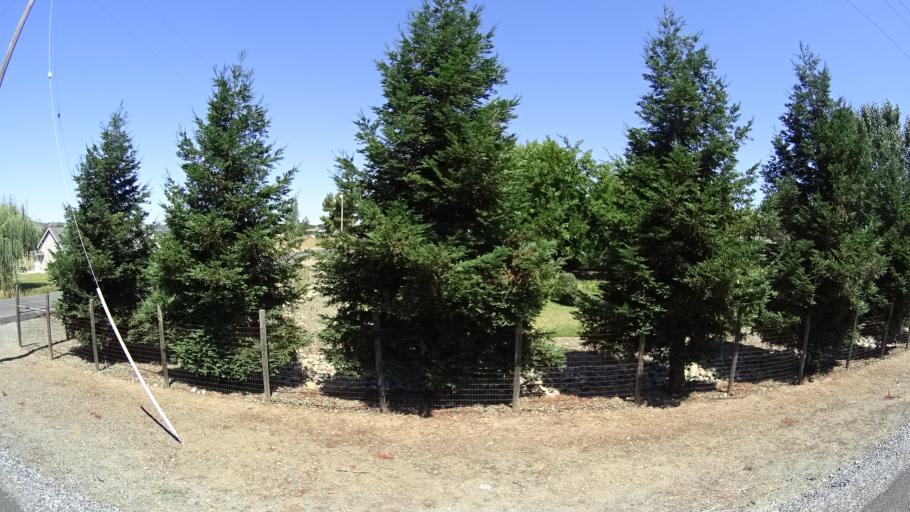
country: US
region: California
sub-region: Calaveras County
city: Copperopolis
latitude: 37.9334
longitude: -120.6406
